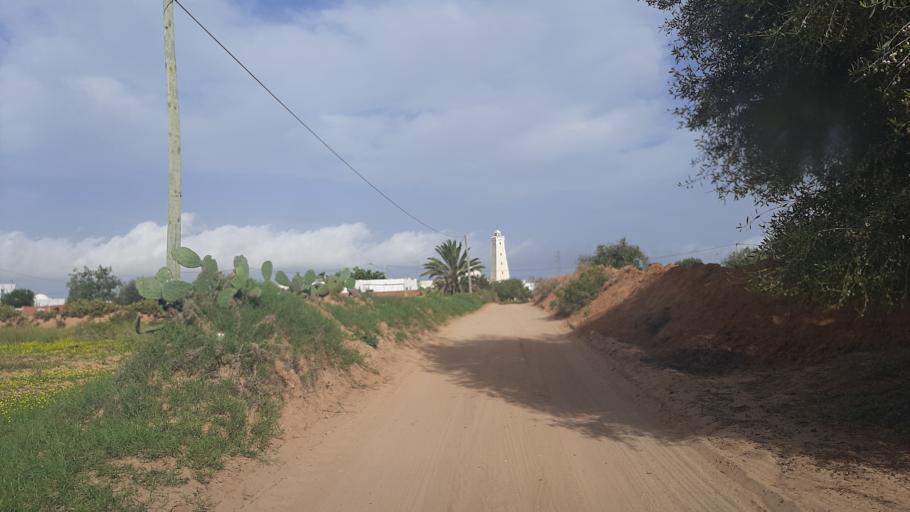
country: TN
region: Madanin
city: Midoun
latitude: 33.7966
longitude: 11.0294
